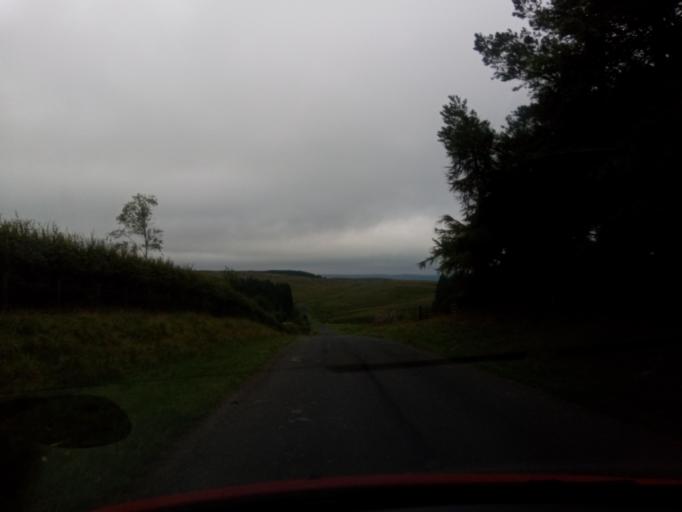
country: GB
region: England
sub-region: Northumberland
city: Otterburn
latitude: 55.2593
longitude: -2.1299
